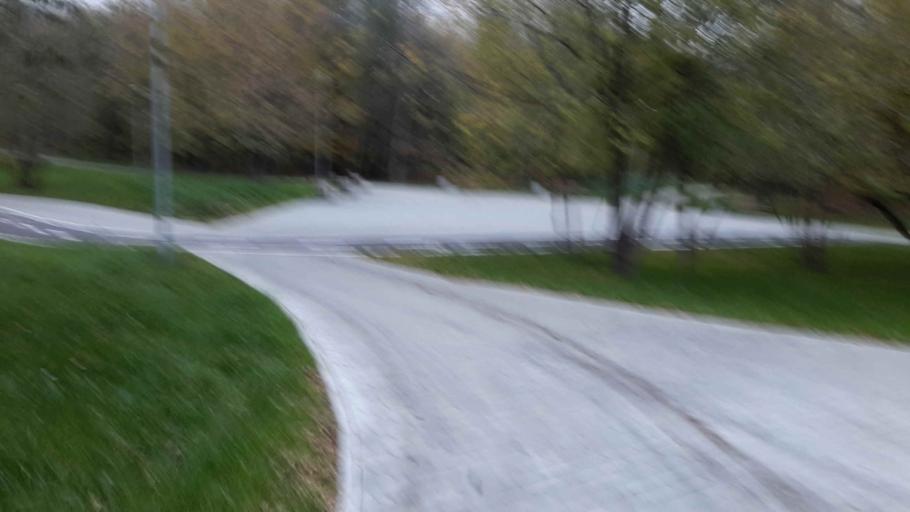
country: RU
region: Moscow
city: Orekhovo-Borisovo
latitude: 55.6302
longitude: 37.7329
